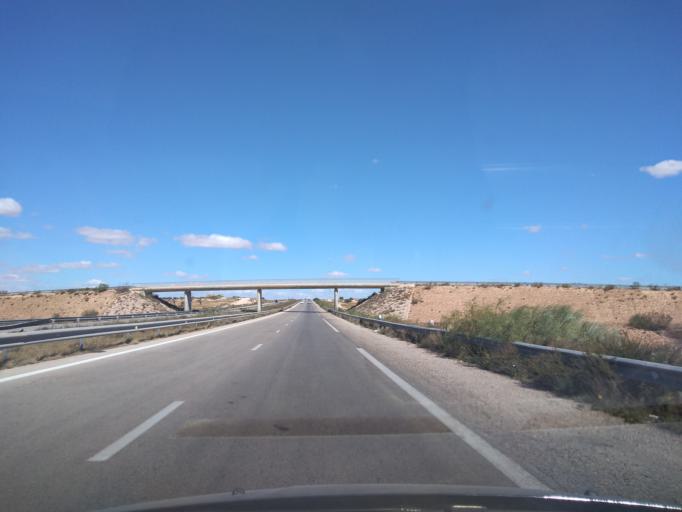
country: TN
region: Safaqis
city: Al Qarmadah
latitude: 34.9255
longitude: 10.7380
